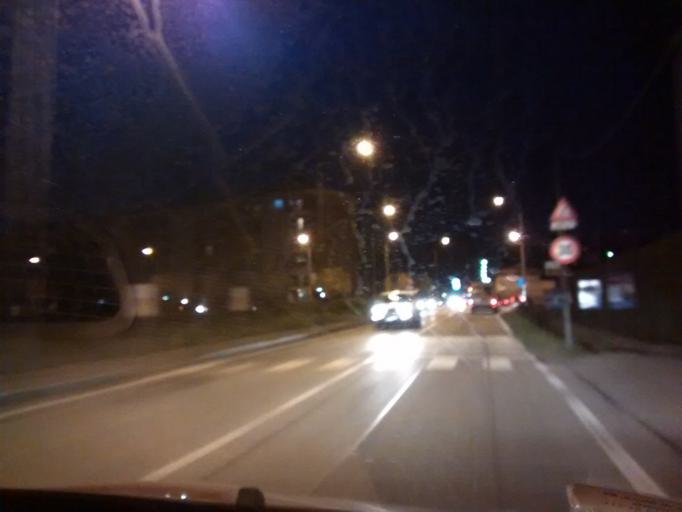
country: IT
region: Piedmont
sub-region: Provincia di Torino
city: Pinerolo
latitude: 44.8755
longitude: 7.3334
